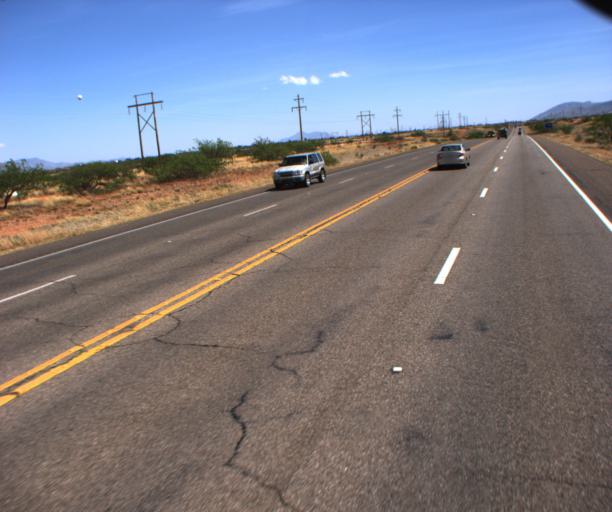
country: US
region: Arizona
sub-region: Cochise County
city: Sierra Vista
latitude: 31.5838
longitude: -110.3198
